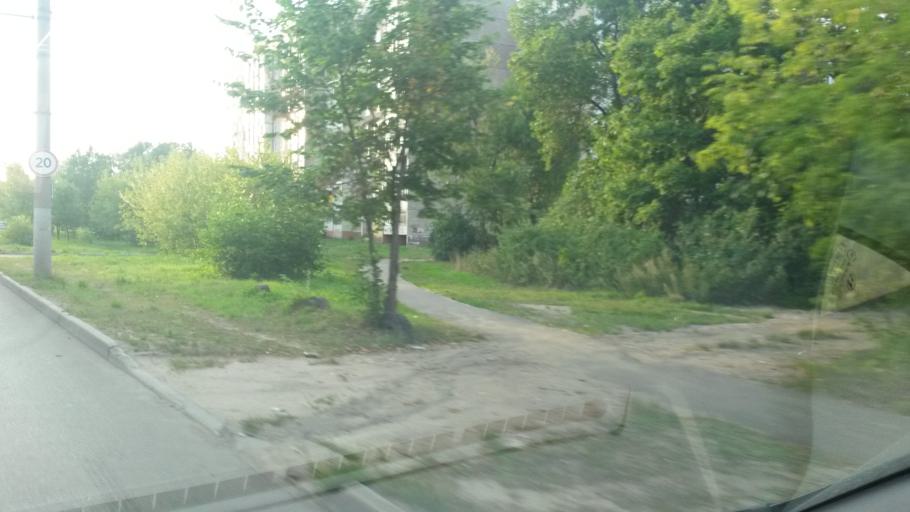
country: RU
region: Ivanovo
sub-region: Gorod Ivanovo
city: Ivanovo
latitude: 57.0104
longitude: 40.9407
